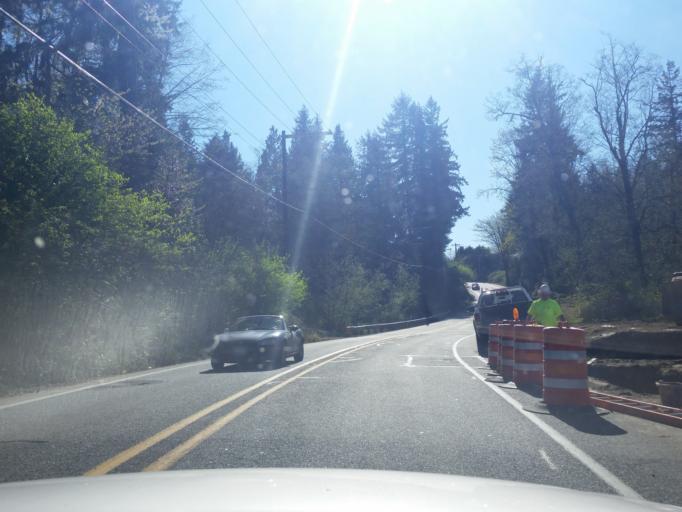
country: US
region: Washington
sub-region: Snohomish County
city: Silver Firs
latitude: 47.8859
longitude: -122.1528
